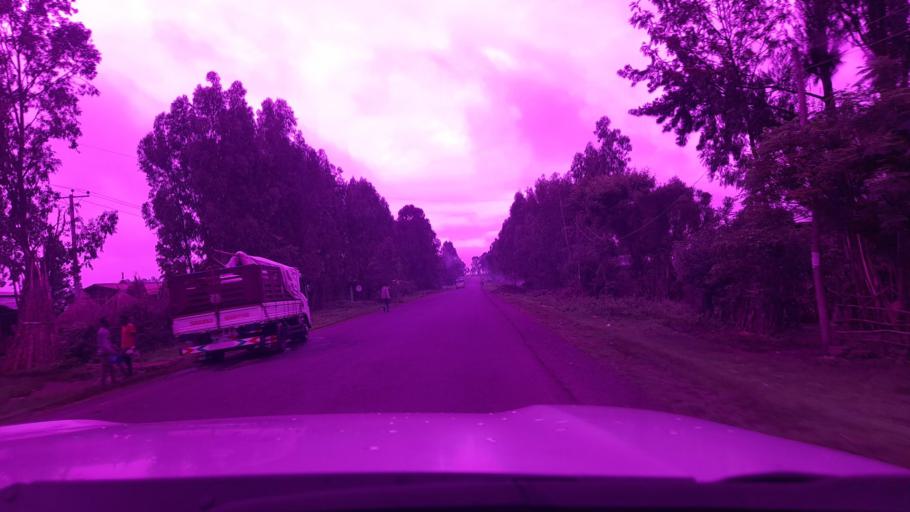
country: ET
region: Oromiya
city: Waliso
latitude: 8.2745
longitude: 37.6678
